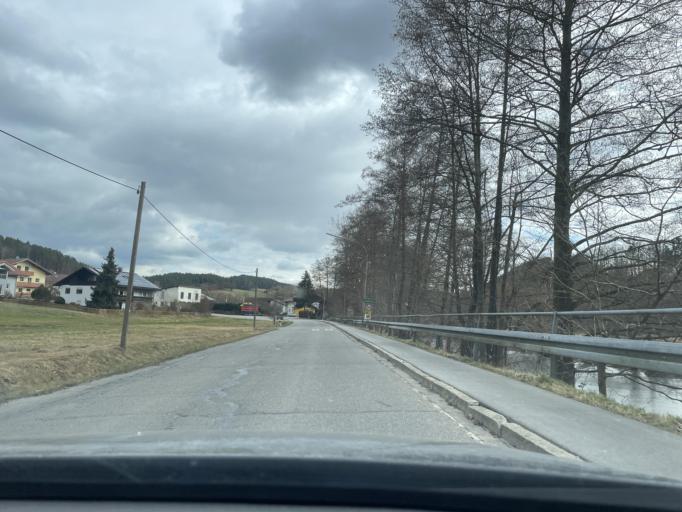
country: DE
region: Bavaria
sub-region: Lower Bavaria
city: Viechtach
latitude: 49.0736
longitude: 12.9038
